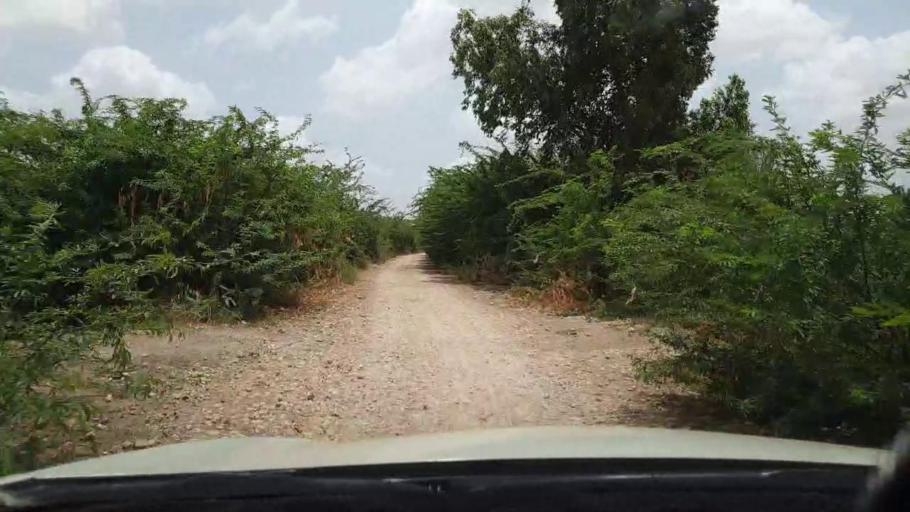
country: PK
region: Sindh
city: Kadhan
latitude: 24.3752
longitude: 68.9286
